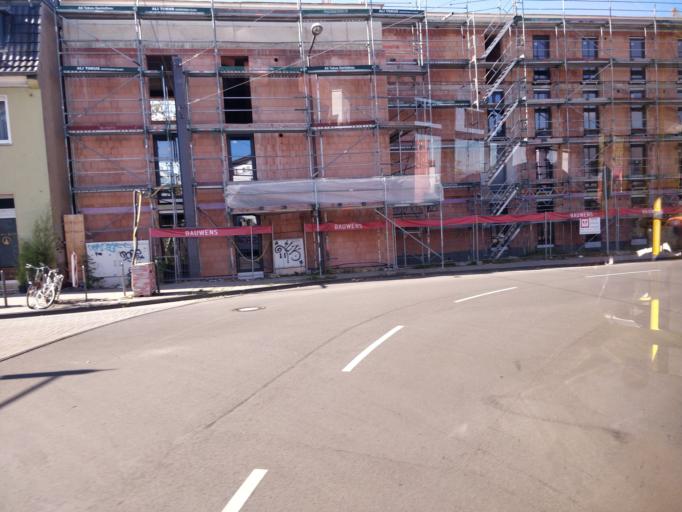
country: DE
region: North Rhine-Westphalia
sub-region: Regierungsbezirk Koln
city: Bilderstoeckchen
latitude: 50.9681
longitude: 6.9055
